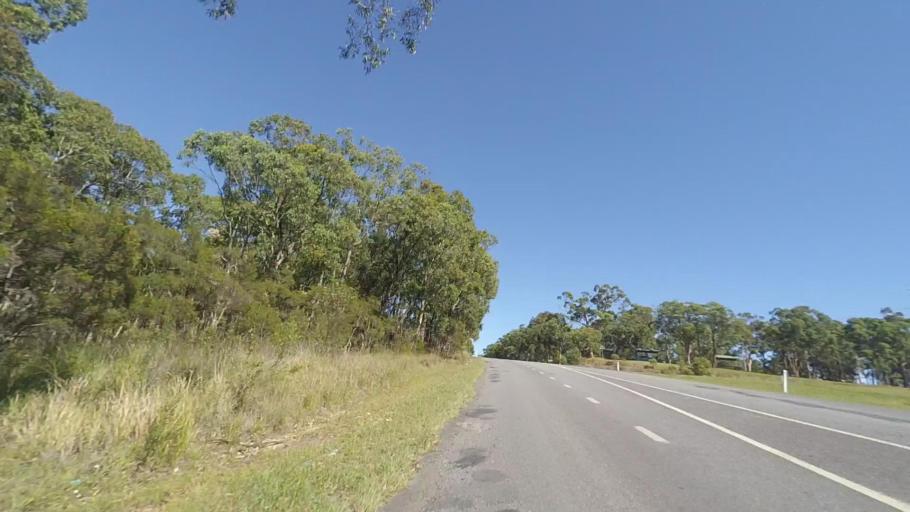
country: AU
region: New South Wales
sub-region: Great Lakes
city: Hawks Nest
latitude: -32.6407
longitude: 152.1447
